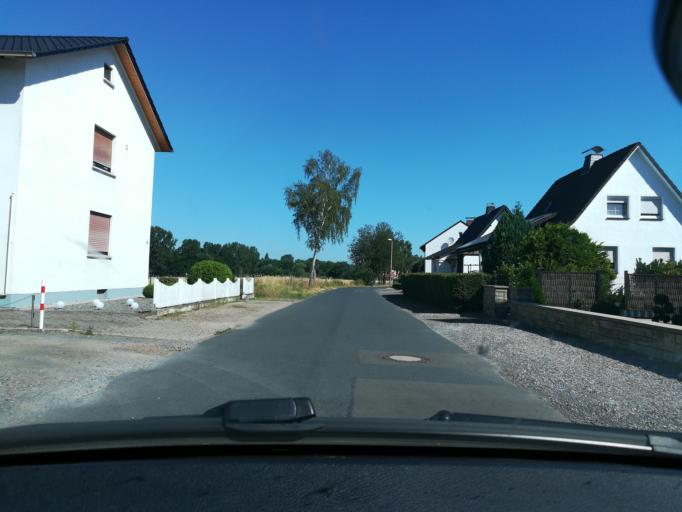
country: DE
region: North Rhine-Westphalia
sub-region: Regierungsbezirk Detmold
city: Minden
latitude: 52.3107
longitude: 8.9292
